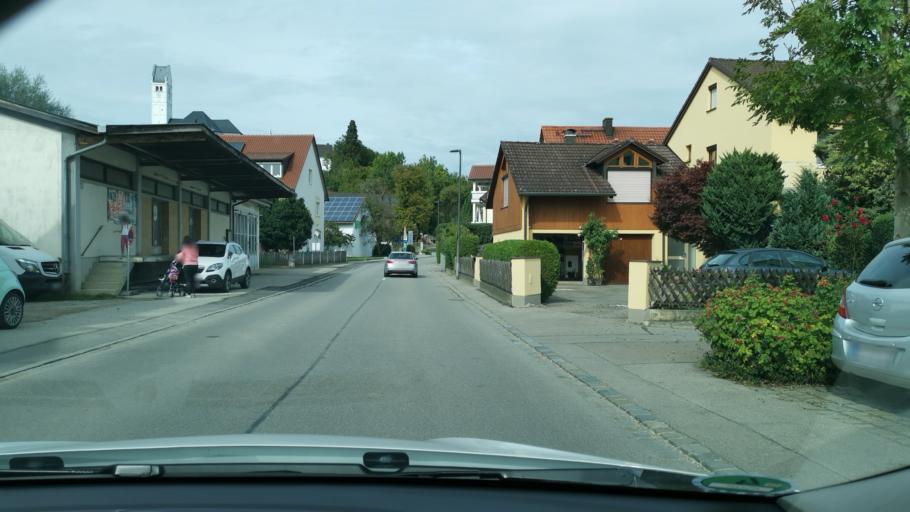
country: DE
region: Bavaria
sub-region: Upper Bavaria
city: Bergkirchen
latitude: 48.2530
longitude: 11.3644
